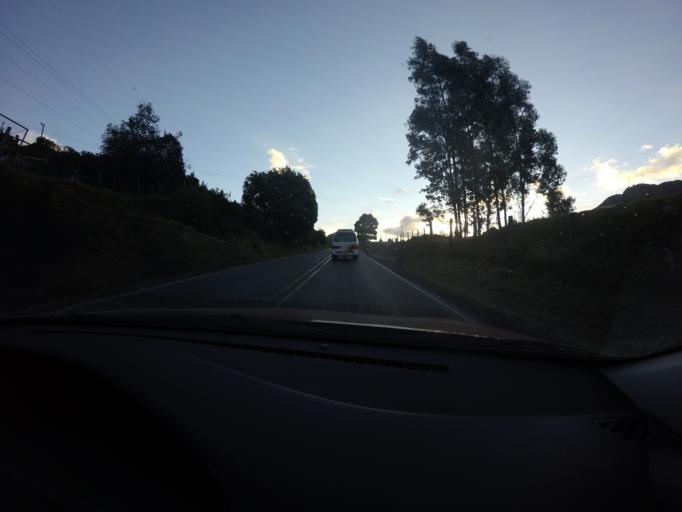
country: CO
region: Cundinamarca
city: Sutatausa
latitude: 5.2041
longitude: -73.8778
